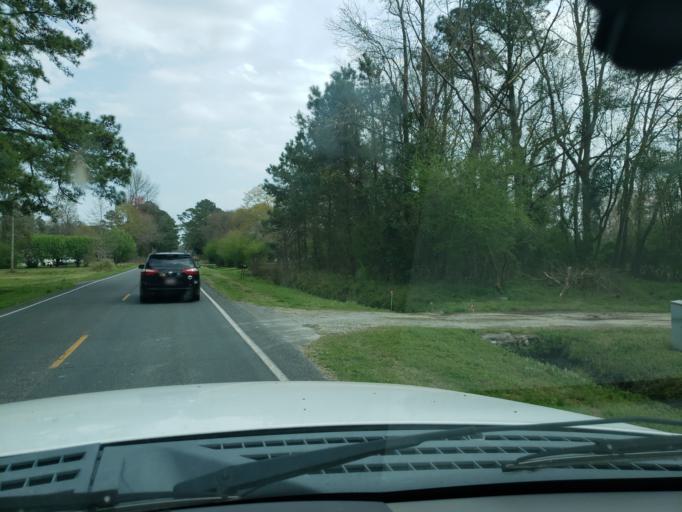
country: US
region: North Carolina
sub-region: Duplin County
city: Beulaville
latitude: 34.7757
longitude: -77.8185
